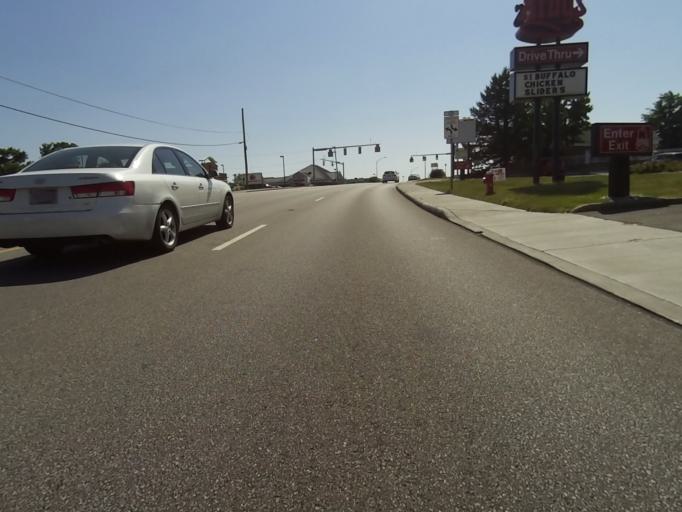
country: US
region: Ohio
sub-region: Summit County
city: Silver Lake
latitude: 41.1636
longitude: -81.4783
